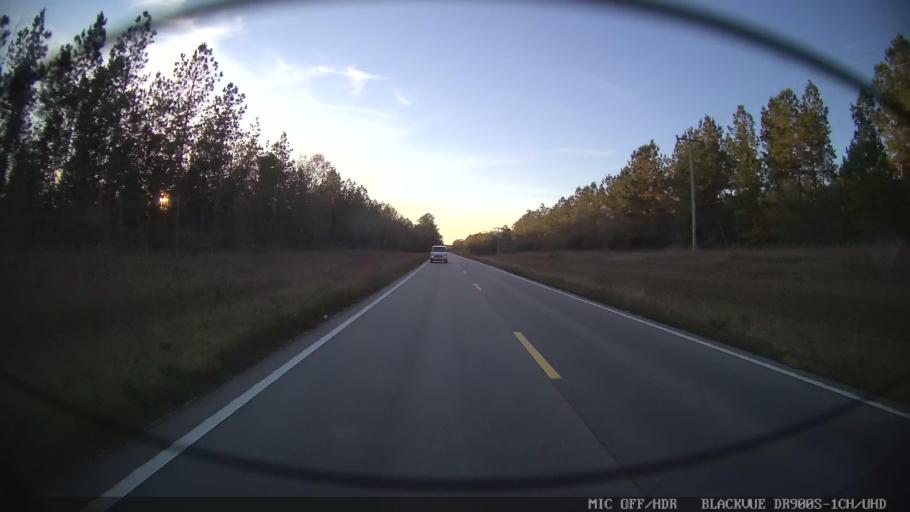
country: US
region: Mississippi
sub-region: Lamar County
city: Lumberton
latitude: 30.9898
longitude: -89.2669
